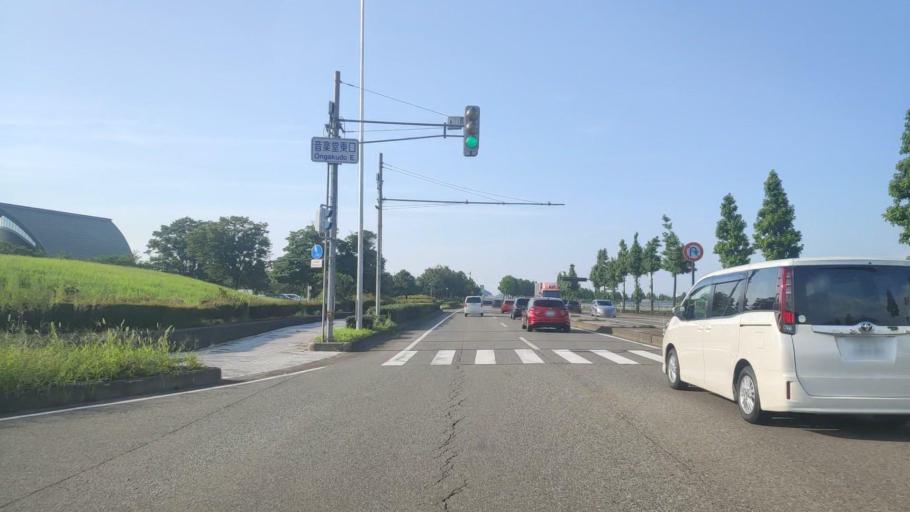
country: JP
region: Fukui
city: Fukui-shi
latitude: 36.0127
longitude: 136.2093
